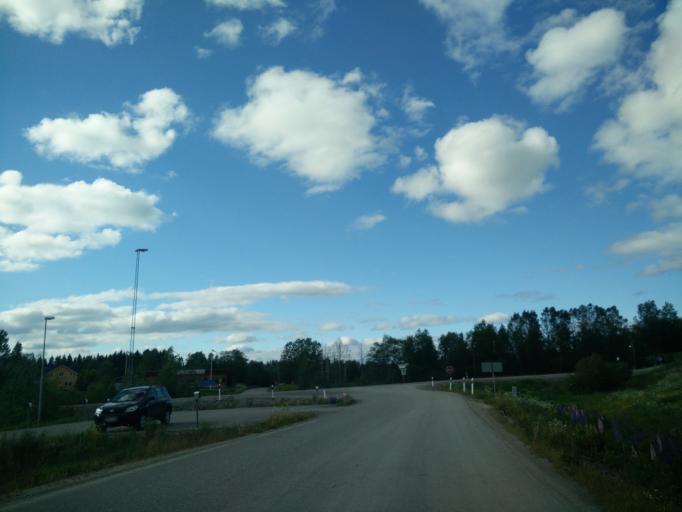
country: SE
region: Vaesternorrland
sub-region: Haernoesands Kommun
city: Haernoesand
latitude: 62.5877
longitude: 17.7886
